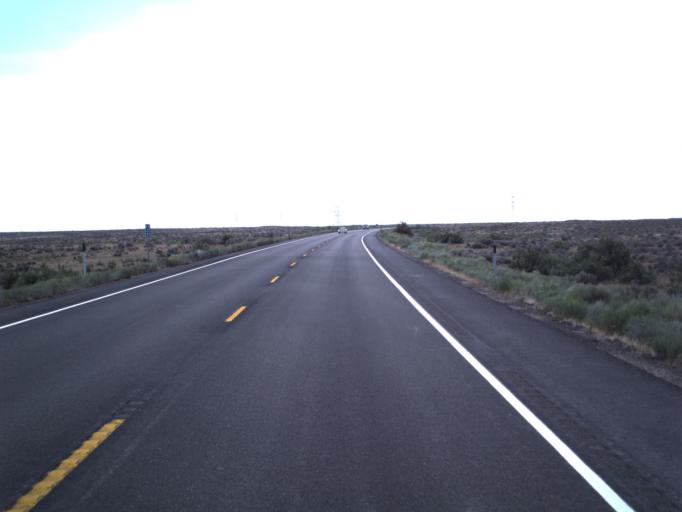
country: US
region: Utah
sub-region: Uintah County
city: Naples
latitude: 40.2397
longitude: -109.4152
